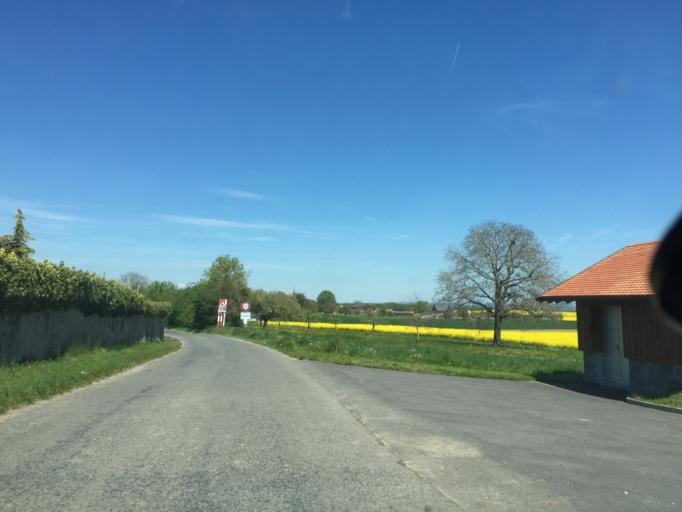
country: CH
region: Vaud
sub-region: Morges District
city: Cuarnens
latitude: 46.6207
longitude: 6.4352
